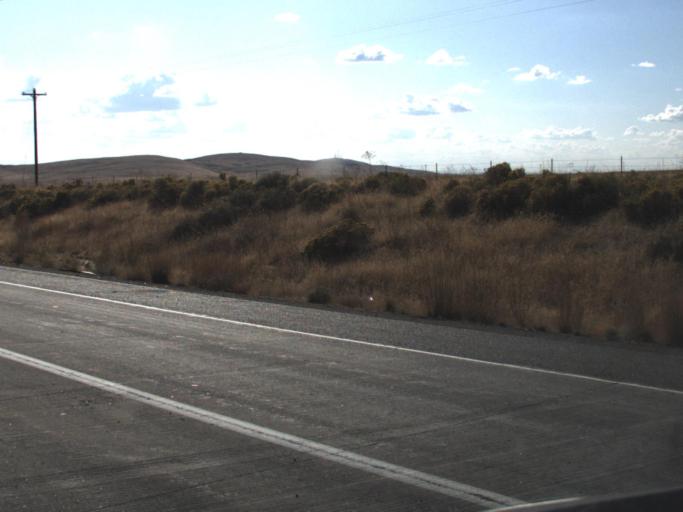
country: US
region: Oregon
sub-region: Umatilla County
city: Umatilla
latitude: 46.0206
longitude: -119.2257
